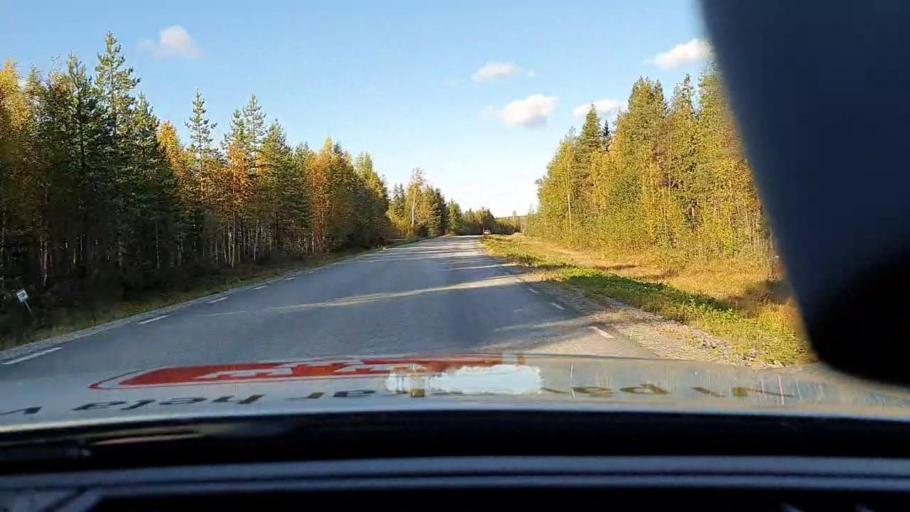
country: SE
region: Norrbotten
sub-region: Pitea Kommun
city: Norrfjarden
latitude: 65.5010
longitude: 21.4762
